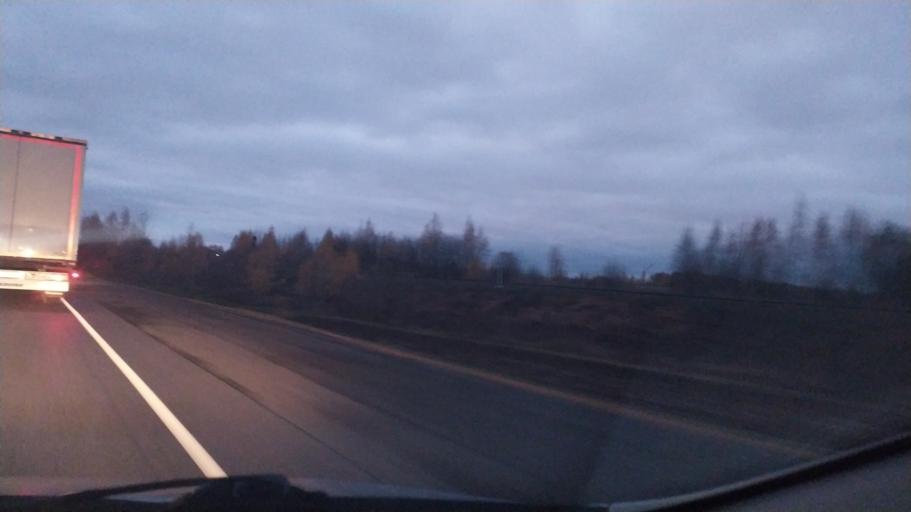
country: RU
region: Chuvashia
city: Kugesi
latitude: 56.0540
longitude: 47.2751
